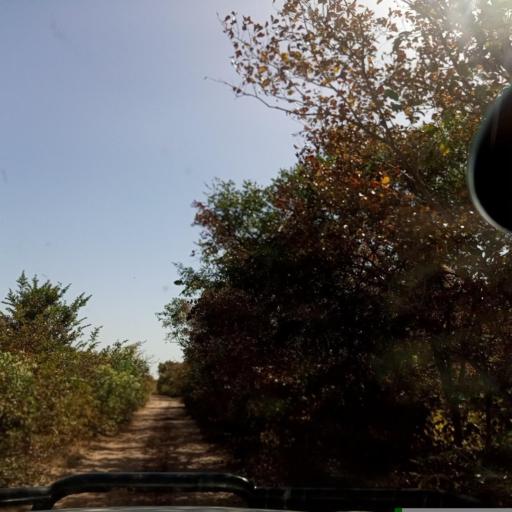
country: ML
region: Koulikoro
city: Koulikoro
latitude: 12.6621
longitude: -7.1970
